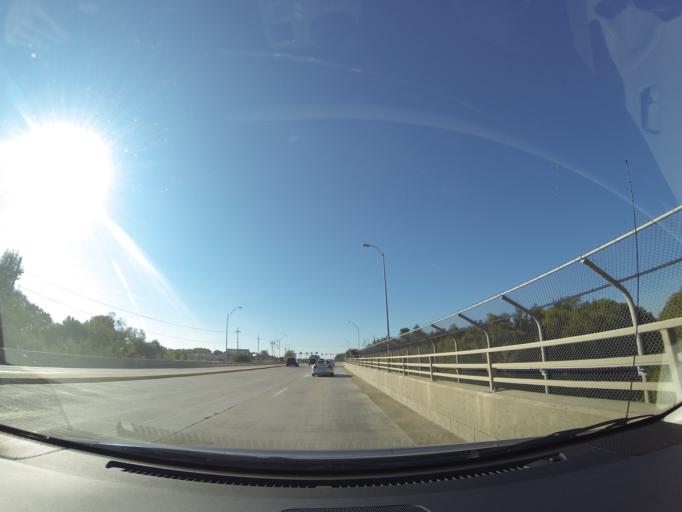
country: US
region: Nebraska
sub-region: Sarpy County
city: Gretna
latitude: 41.1490
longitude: -96.2391
